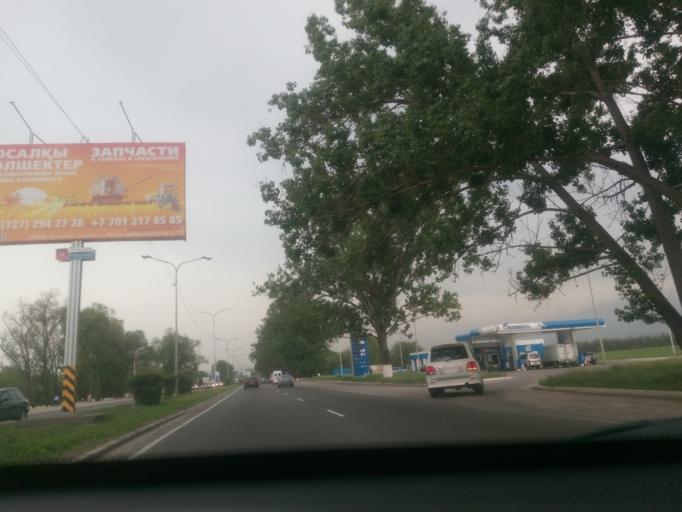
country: KZ
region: Almaty Oblysy
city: Burunday
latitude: 43.2278
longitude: 76.7520
